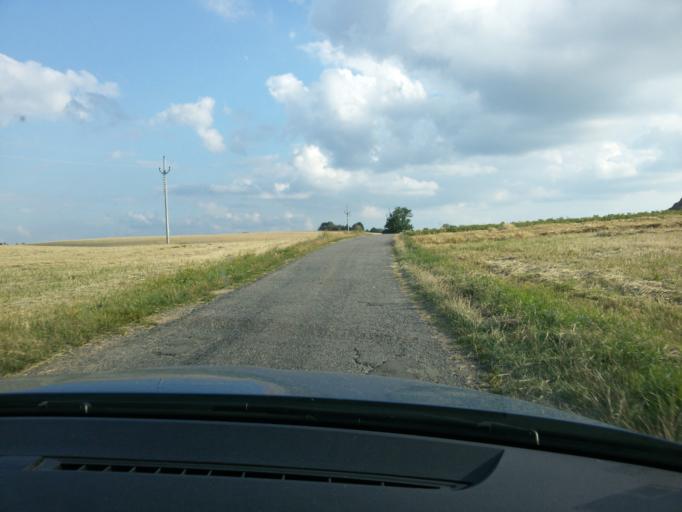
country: CZ
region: South Moravian
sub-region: Okres Brno-Venkov
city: Lomnice
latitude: 49.4776
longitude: 16.4286
